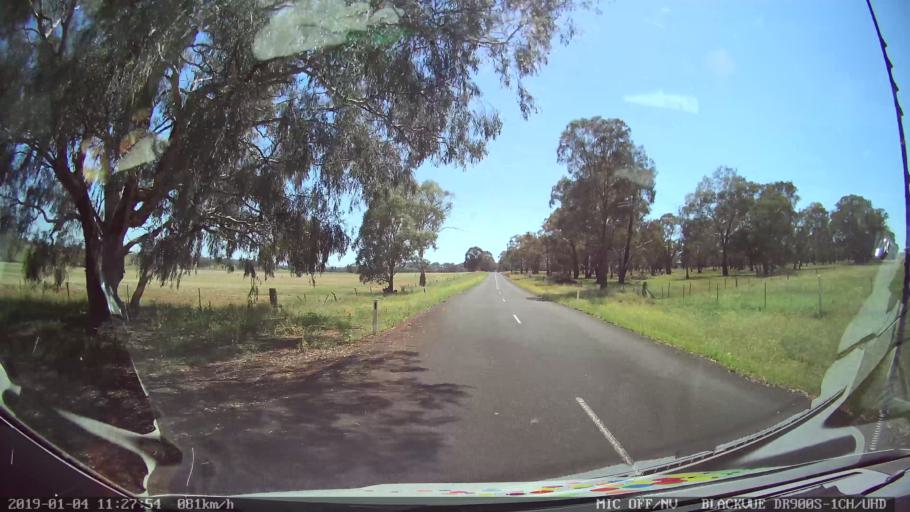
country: AU
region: New South Wales
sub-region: Cabonne
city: Molong
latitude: -33.1050
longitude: 148.7671
